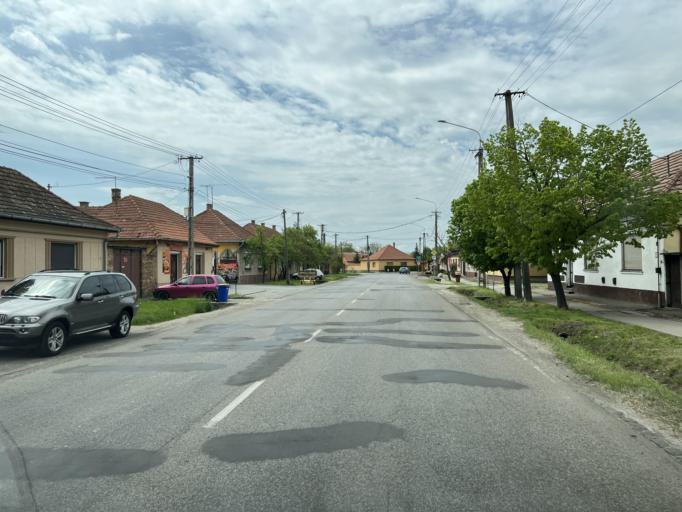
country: HU
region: Pest
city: Cegled
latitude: 47.1635
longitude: 19.8003
